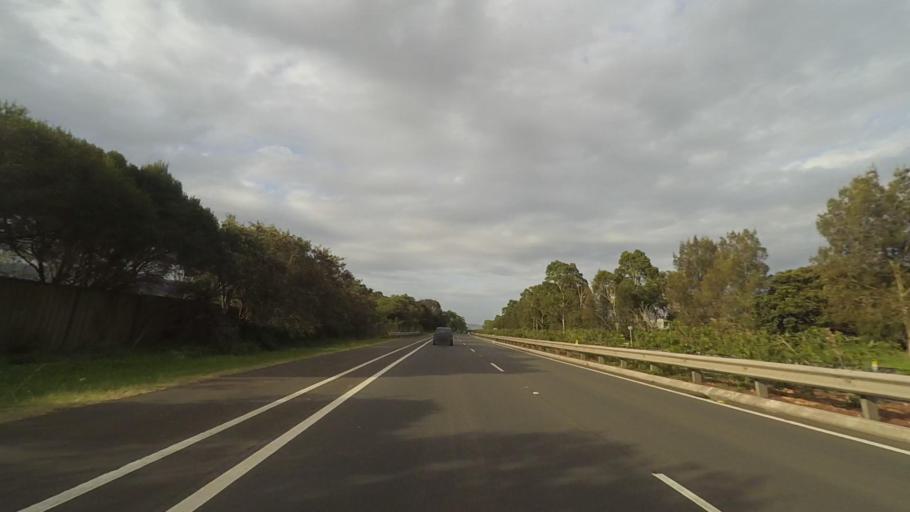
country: AU
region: New South Wales
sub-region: Wollongong
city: Fairy Meadow
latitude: -34.4006
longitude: 150.8934
